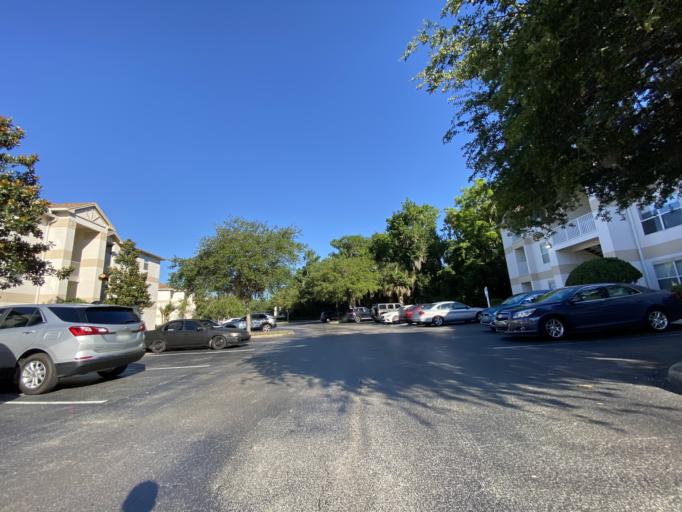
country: US
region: Florida
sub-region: Volusia County
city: Port Orange
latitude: 29.1417
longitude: -80.9959
